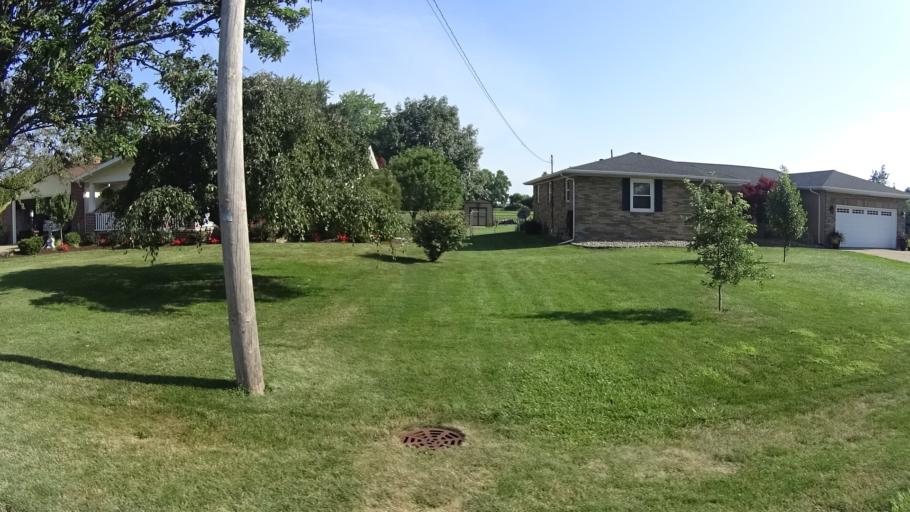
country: US
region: Ohio
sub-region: Erie County
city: Sandusky
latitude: 41.4484
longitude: -82.7796
